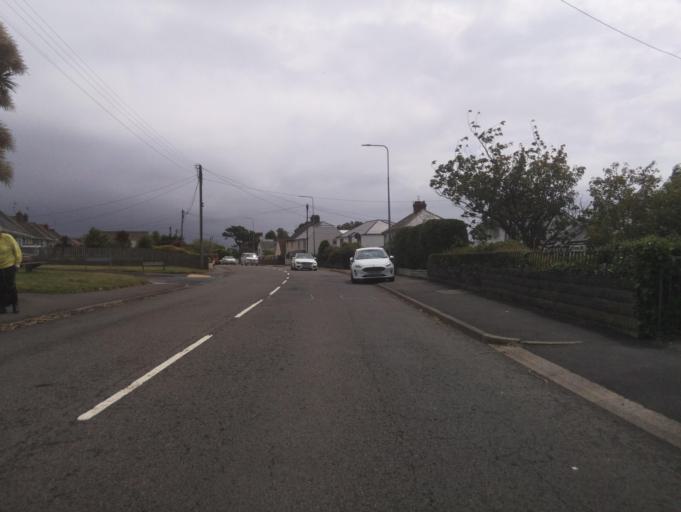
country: GB
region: Wales
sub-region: Vale of Glamorgan
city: Dinas Powys
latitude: 51.4044
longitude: -3.2105
